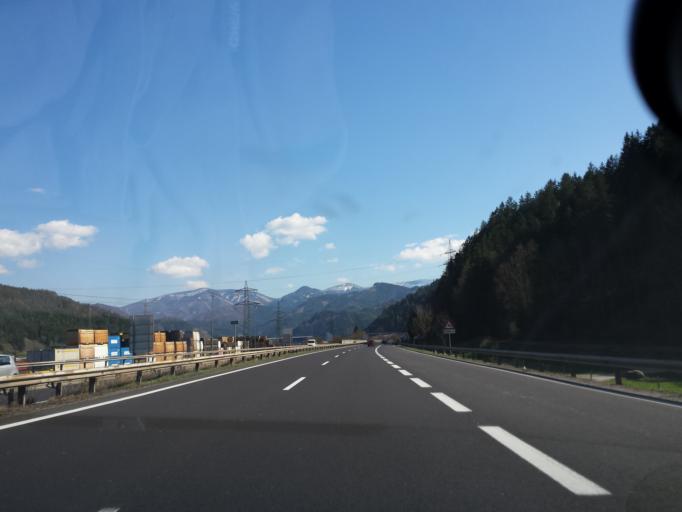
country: AT
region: Styria
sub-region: Politischer Bezirk Leoben
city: Traboch
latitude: 47.3633
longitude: 14.9983
